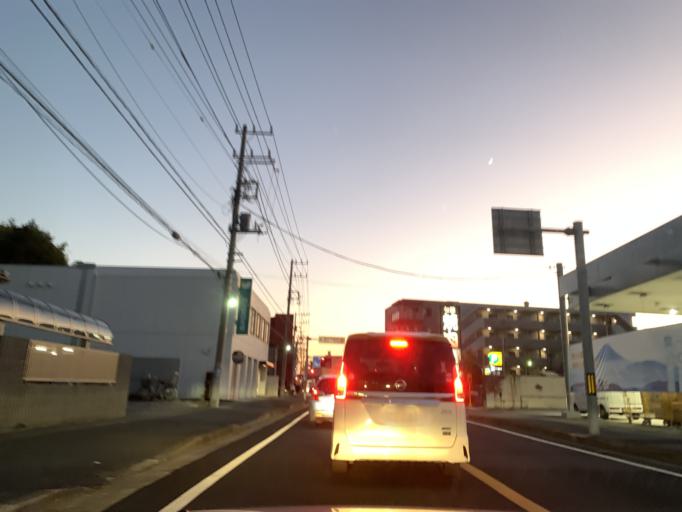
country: JP
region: Chiba
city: Nagareyama
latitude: 35.8588
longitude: 139.9019
